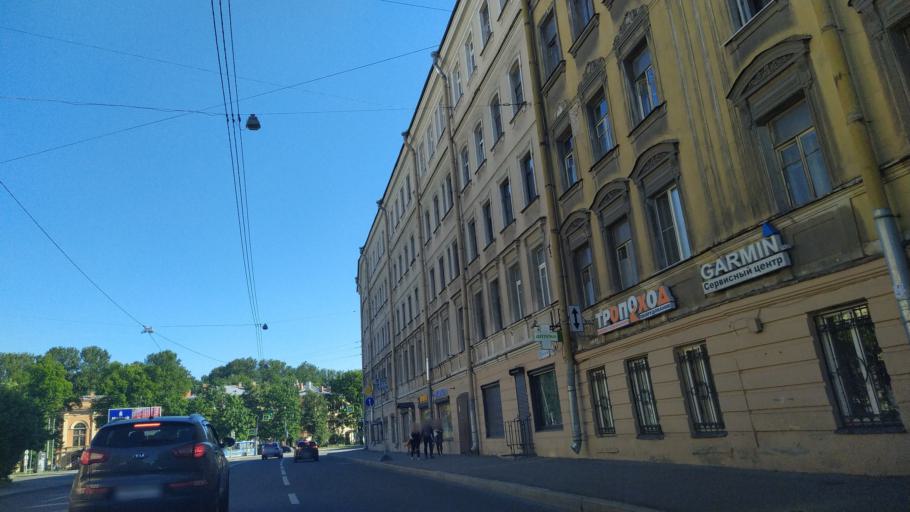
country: RU
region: Leningrad
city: Finlyandskiy
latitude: 59.9603
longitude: 30.3452
